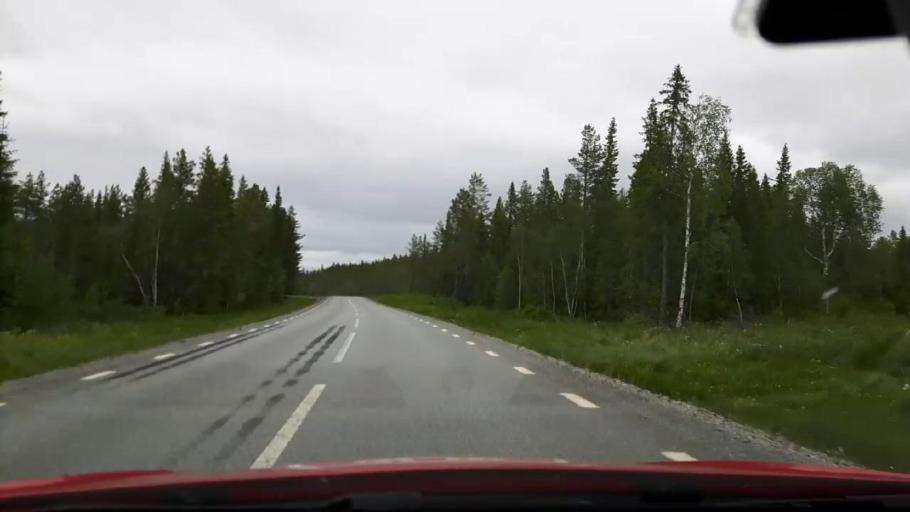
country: SE
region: Jaemtland
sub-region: OEstersunds Kommun
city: Lit
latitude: 63.6929
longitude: 14.6814
